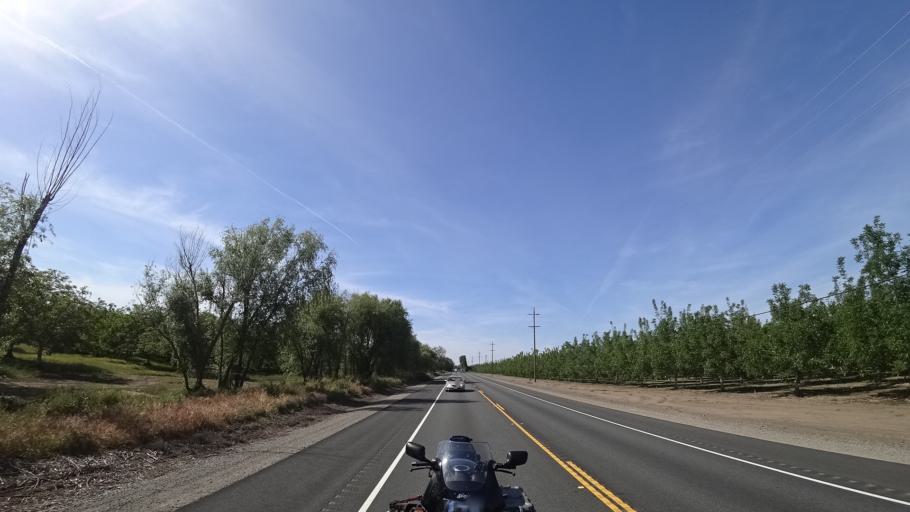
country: US
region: California
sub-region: Glenn County
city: Hamilton City
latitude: 39.8727
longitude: -121.9680
